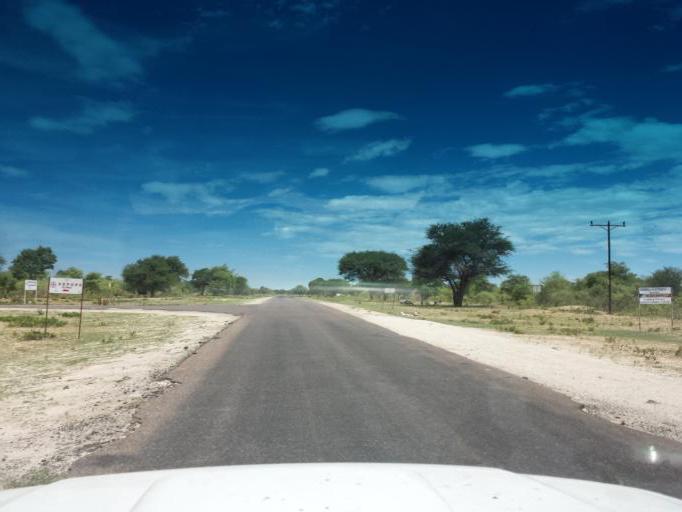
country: BW
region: North West
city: Shakawe
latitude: -18.7484
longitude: 22.1730
